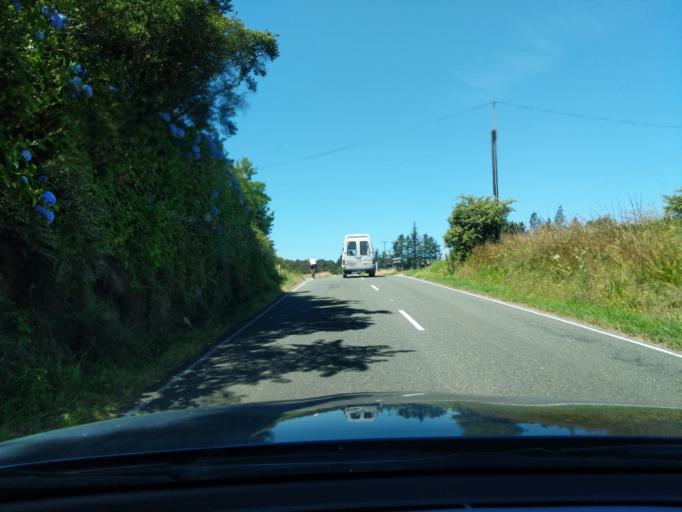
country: NZ
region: Tasman
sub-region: Tasman District
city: Takaka
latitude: -40.6952
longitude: 172.6338
